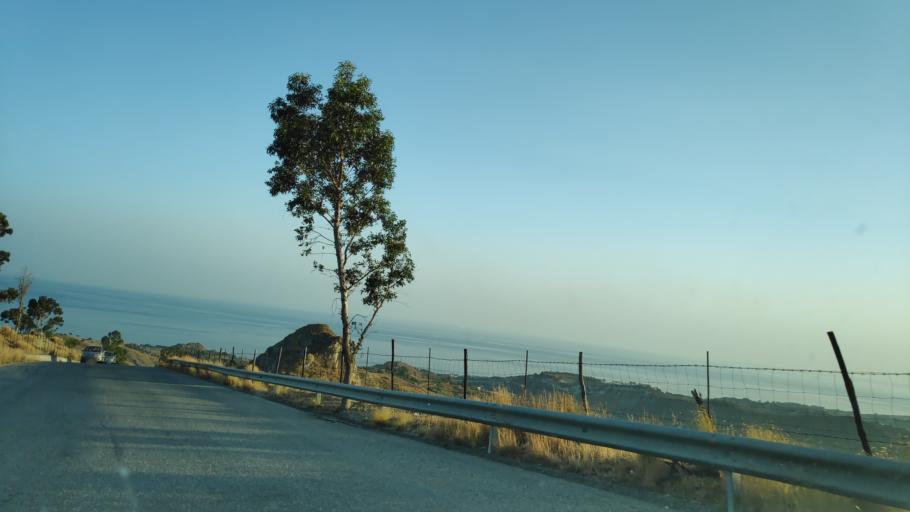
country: IT
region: Calabria
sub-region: Provincia di Reggio Calabria
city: Bova Marina
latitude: 37.9533
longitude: 15.9207
